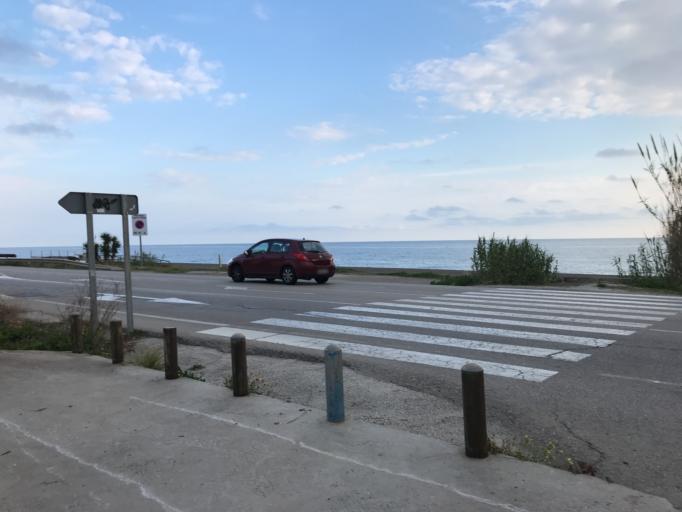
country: ES
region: Andalusia
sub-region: Provincia de Malaga
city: Valdes
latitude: 36.7152
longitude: -4.2050
